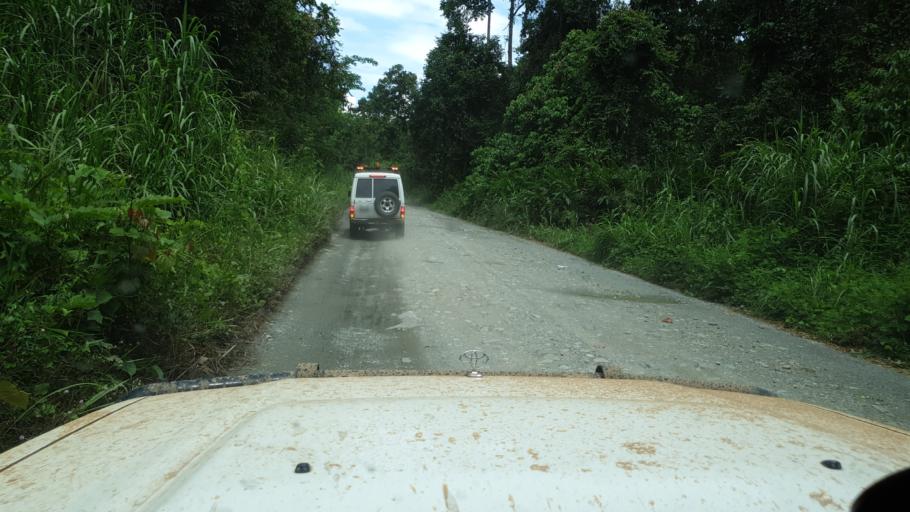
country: PG
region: Northern Province
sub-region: Sohe
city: Kokoda
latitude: -8.9164
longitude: 147.9187
